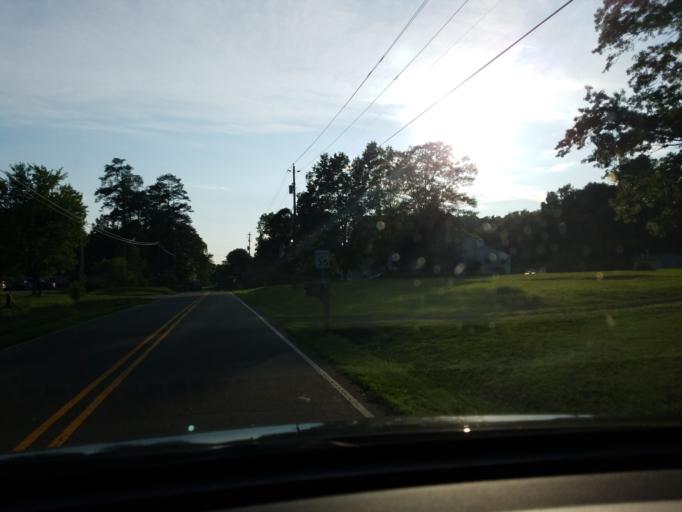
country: US
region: North Carolina
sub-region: Granville County
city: Butner
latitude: 36.1685
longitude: -78.8714
